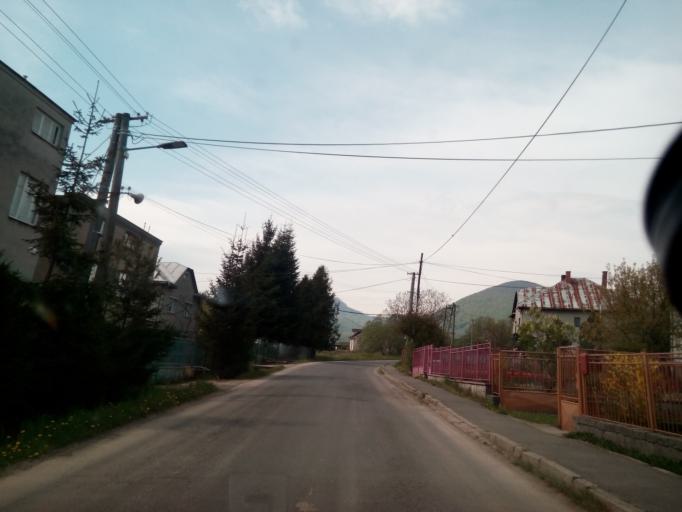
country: SK
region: Presovsky
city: Giraltovce
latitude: 48.9953
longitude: 21.5279
